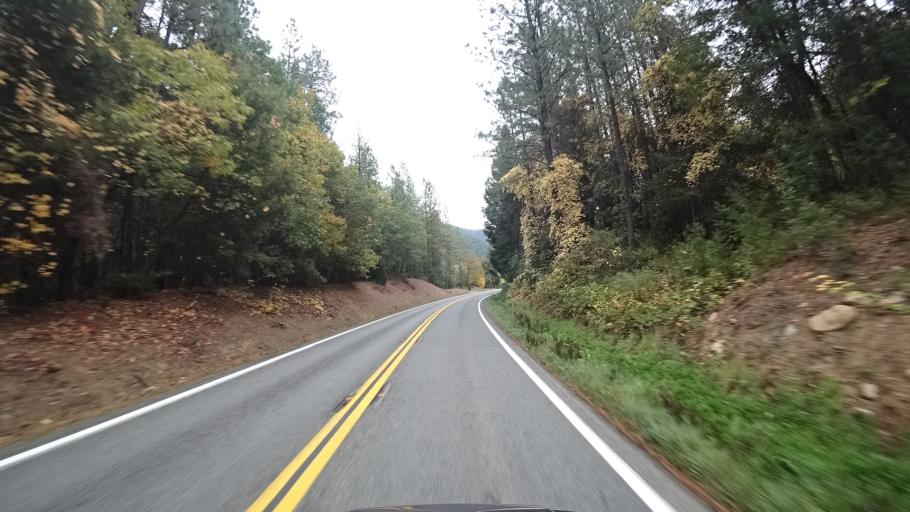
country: US
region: California
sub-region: Siskiyou County
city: Happy Camp
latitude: 41.8355
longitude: -123.1748
